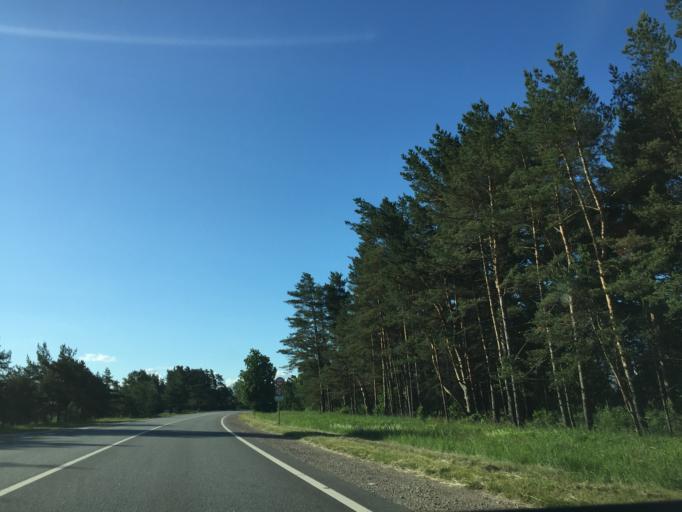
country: LV
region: Ventspils
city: Ventspils
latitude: 57.3991
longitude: 21.6916
